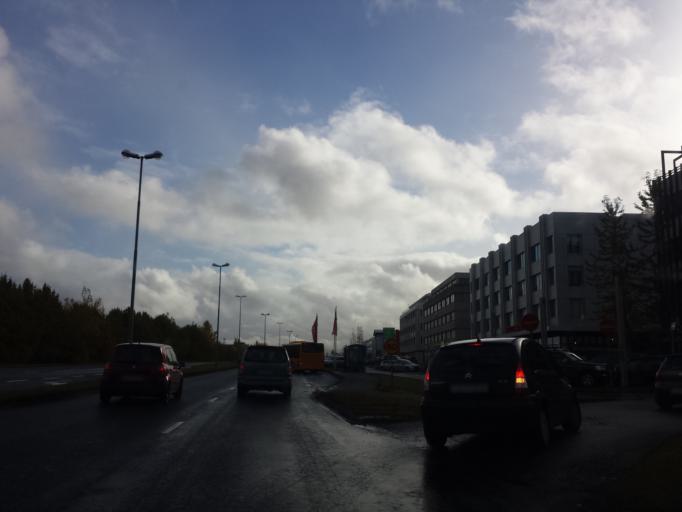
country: IS
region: Capital Region
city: Reykjavik
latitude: 64.1385
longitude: -21.8785
